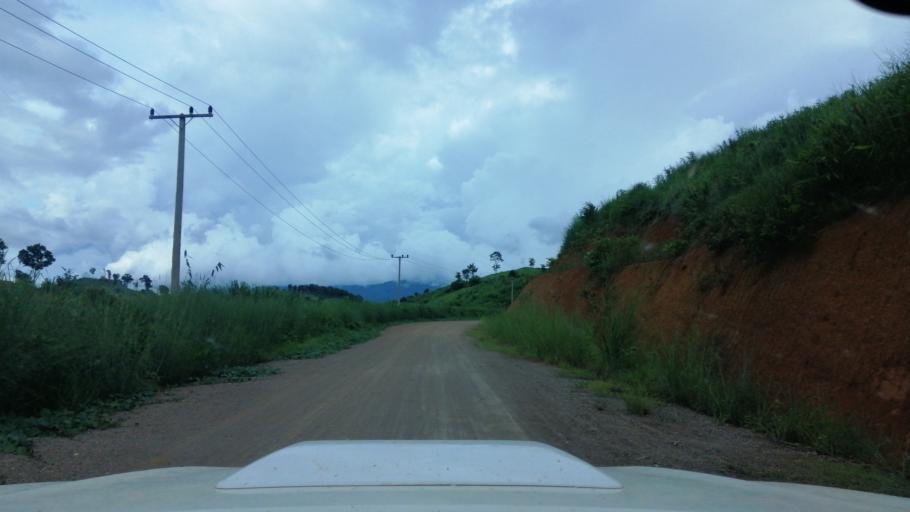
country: TH
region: Nan
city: Song Khwae
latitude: 19.5485
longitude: 100.6997
